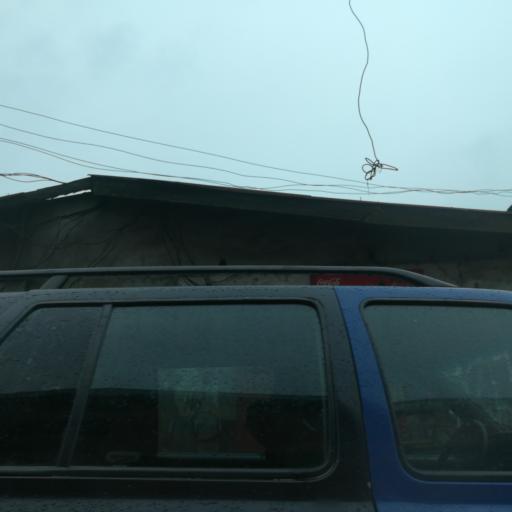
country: NG
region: Rivers
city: Port Harcourt
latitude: 4.8023
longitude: 6.9916
